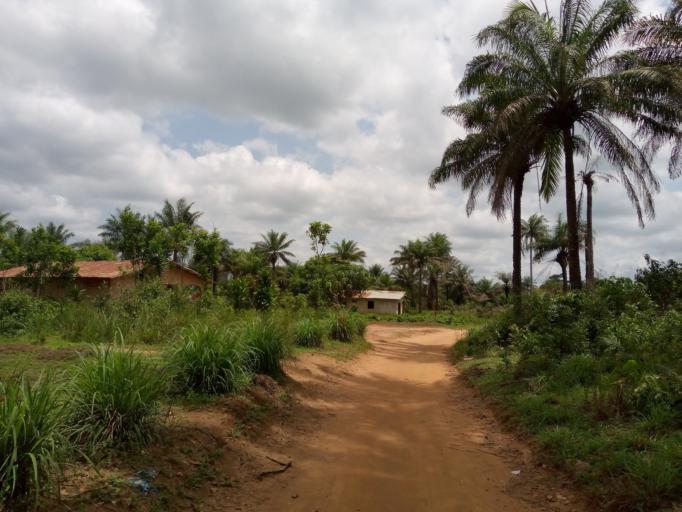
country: SL
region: Western Area
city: Waterloo
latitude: 8.4011
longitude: -12.9487
